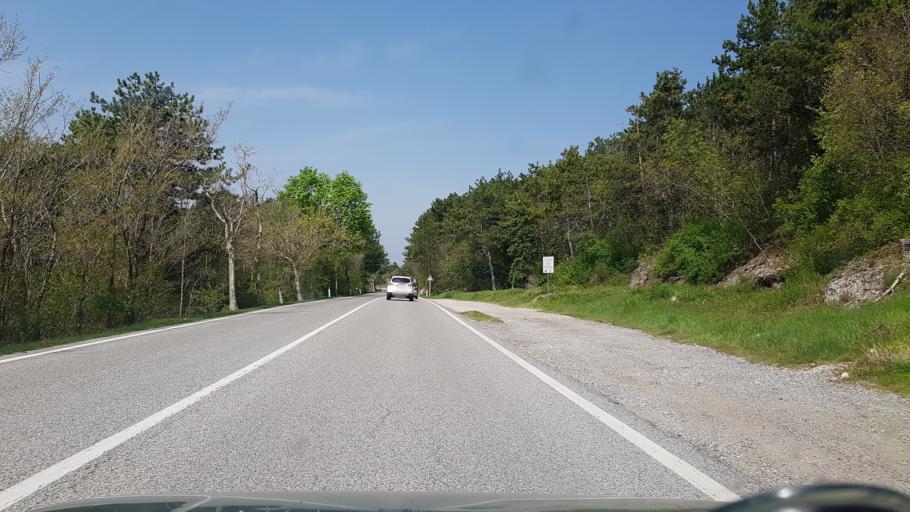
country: IT
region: Friuli Venezia Giulia
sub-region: Provincia di Trieste
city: Dolina
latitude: 45.6302
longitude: 13.8915
